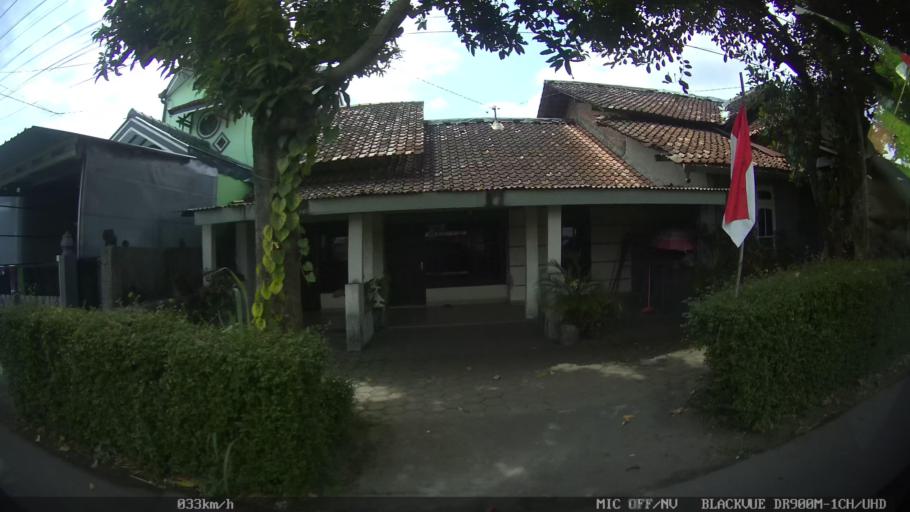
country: ID
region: Daerah Istimewa Yogyakarta
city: Depok
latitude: -7.7769
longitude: 110.4643
